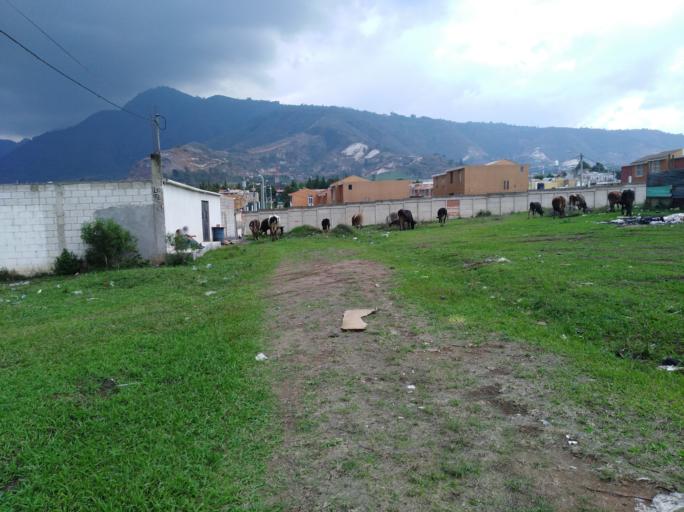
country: GT
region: Guatemala
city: Villa Nueva
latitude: 14.5251
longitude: -90.6246
